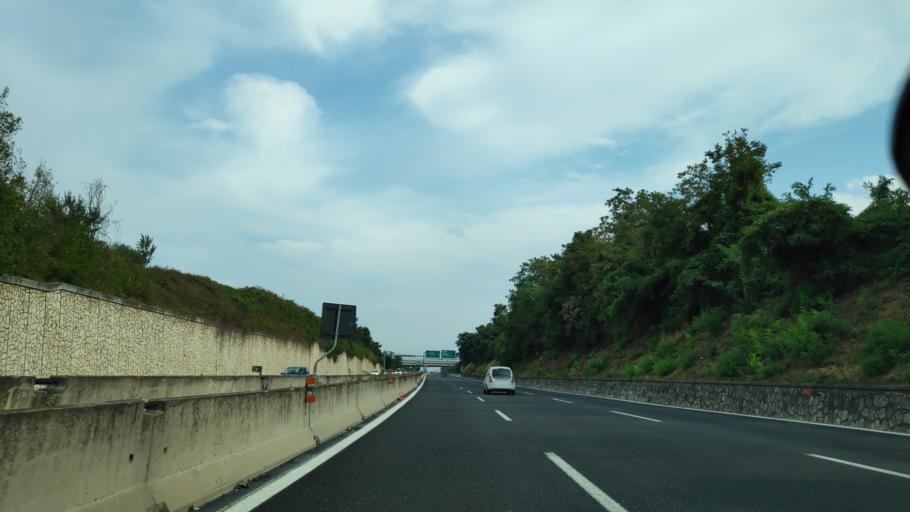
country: IT
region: Latium
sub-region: Citta metropolitana di Roma Capitale
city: Fiano Romano
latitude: 42.1781
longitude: 12.6035
